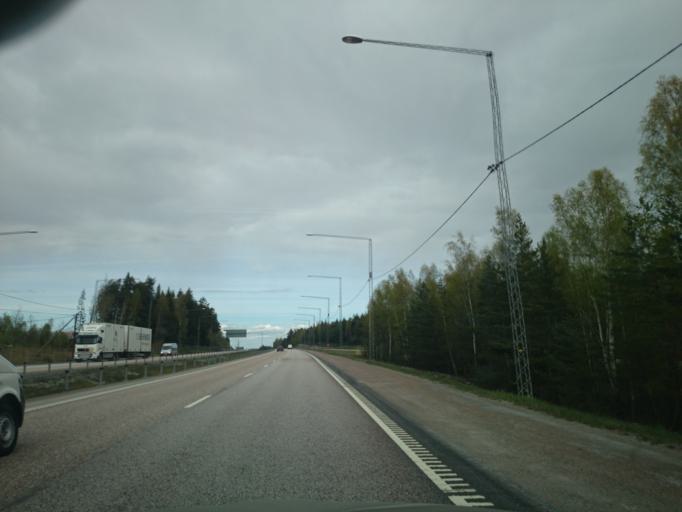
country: SE
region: Stockholm
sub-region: Sigtuna Kommun
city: Rosersberg
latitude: 59.6207
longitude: 17.9012
